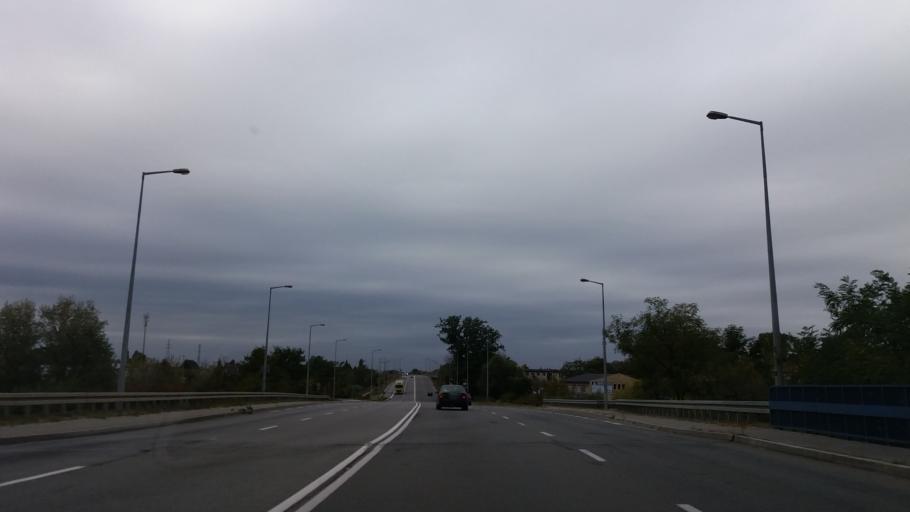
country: PL
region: Lubusz
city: Gorzow Wielkopolski
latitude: 52.7269
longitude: 15.2505
